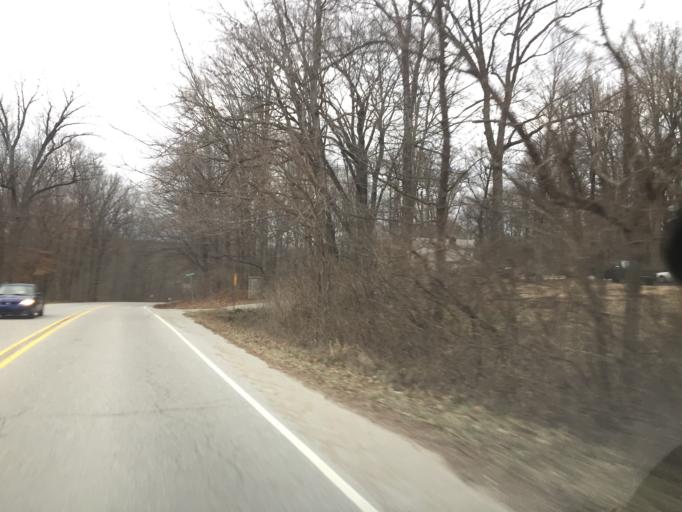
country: US
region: Indiana
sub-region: Monroe County
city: Bloomington
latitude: 39.1977
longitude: -86.5583
